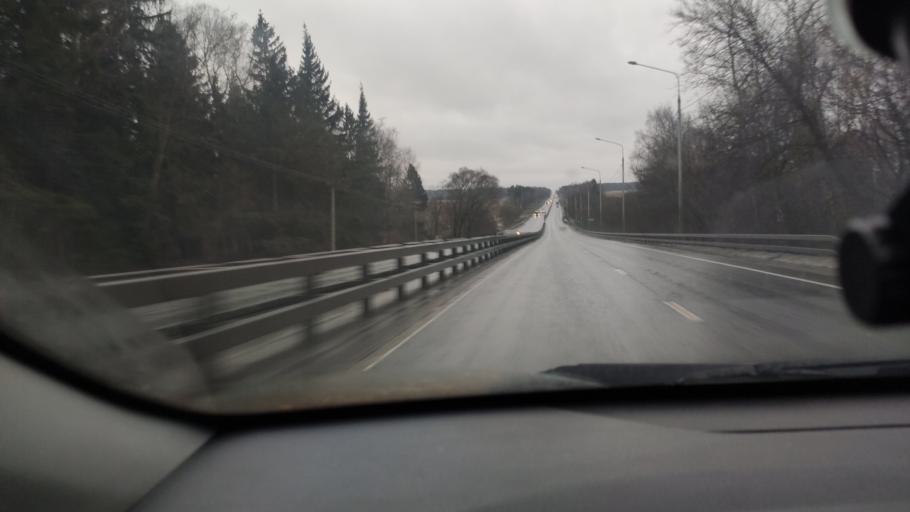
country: RU
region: Moskovskaya
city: Troitsk
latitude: 55.3423
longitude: 37.3131
